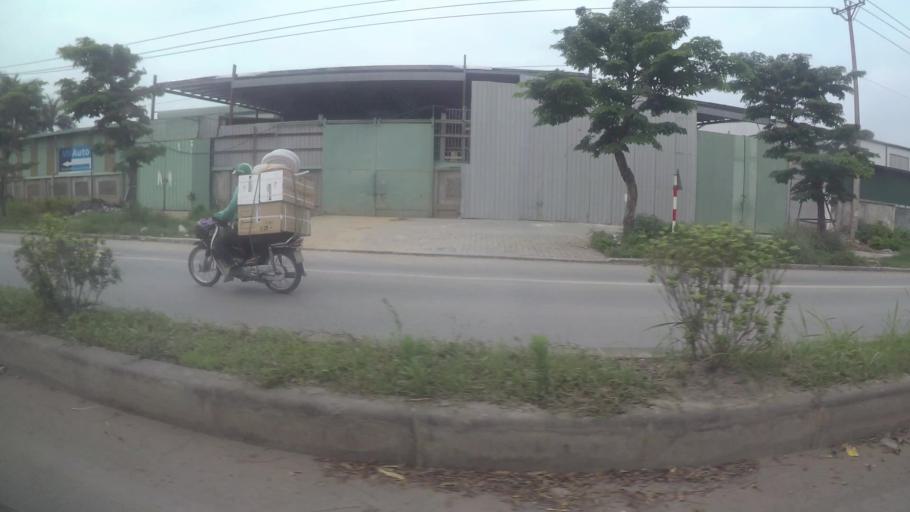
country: VN
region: Ha Noi
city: Cau Dien
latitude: 21.0402
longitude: 105.7404
